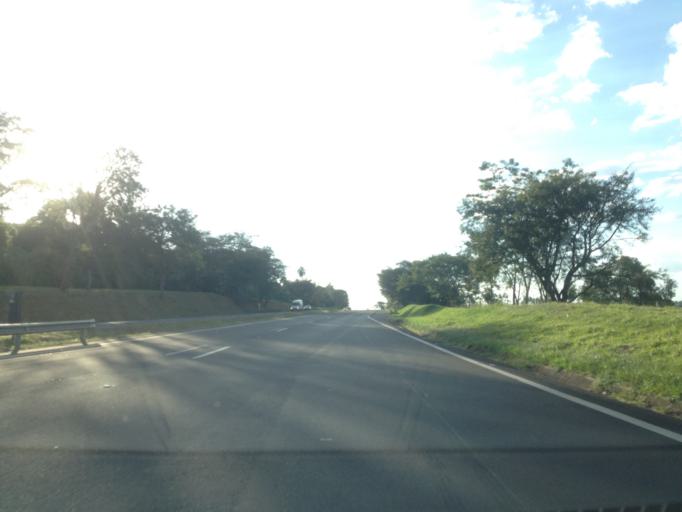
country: BR
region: Sao Paulo
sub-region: Brotas
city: Brotas
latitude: -22.2542
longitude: -48.2456
